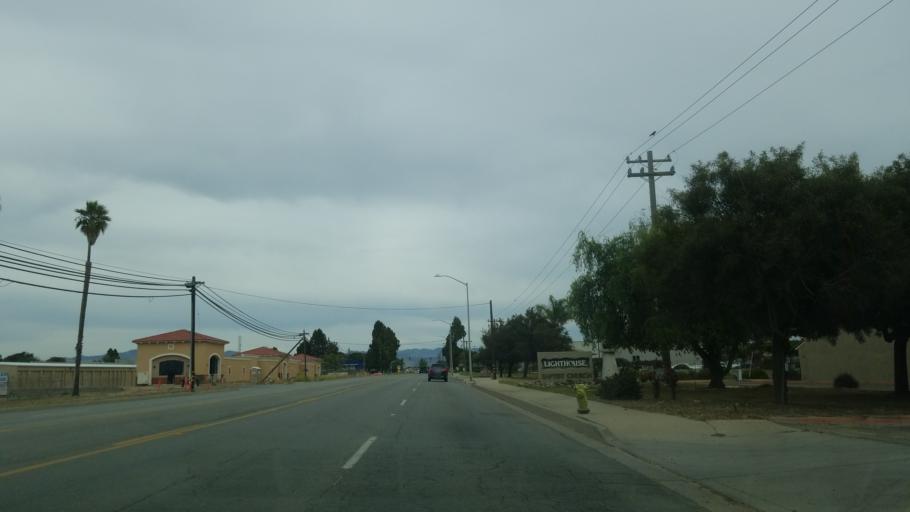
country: US
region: California
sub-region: Santa Barbara County
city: Santa Maria
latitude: 34.9207
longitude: -120.4583
